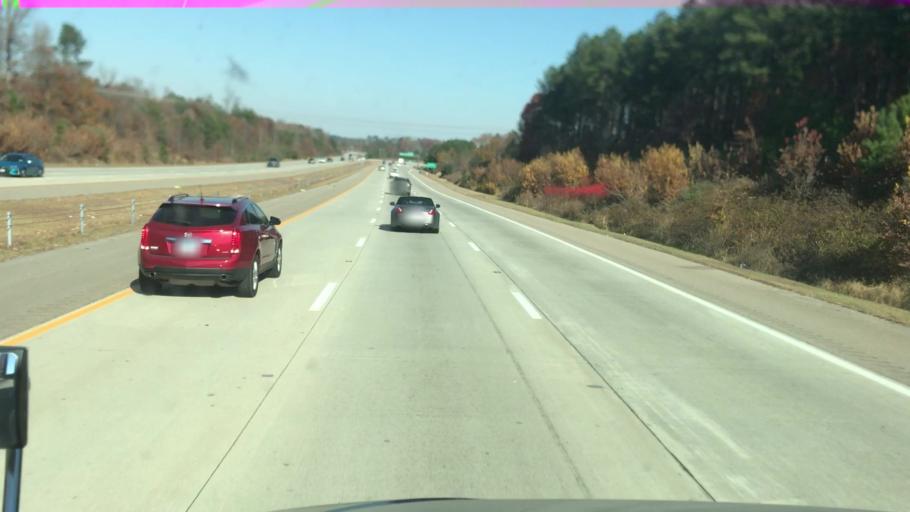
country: US
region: North Carolina
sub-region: Wake County
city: Knightdale
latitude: 35.7740
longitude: -78.4478
